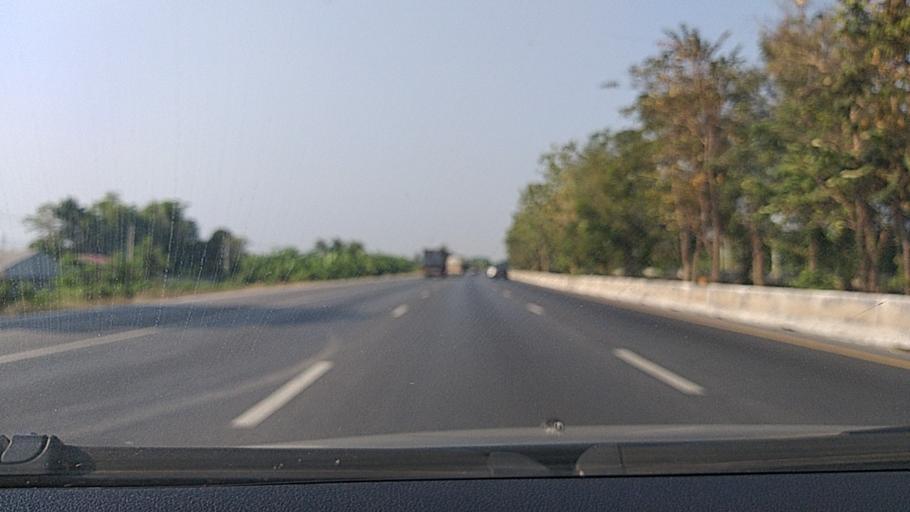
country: TH
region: Ang Thong
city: Chaiyo
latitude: 14.7033
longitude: 100.4556
